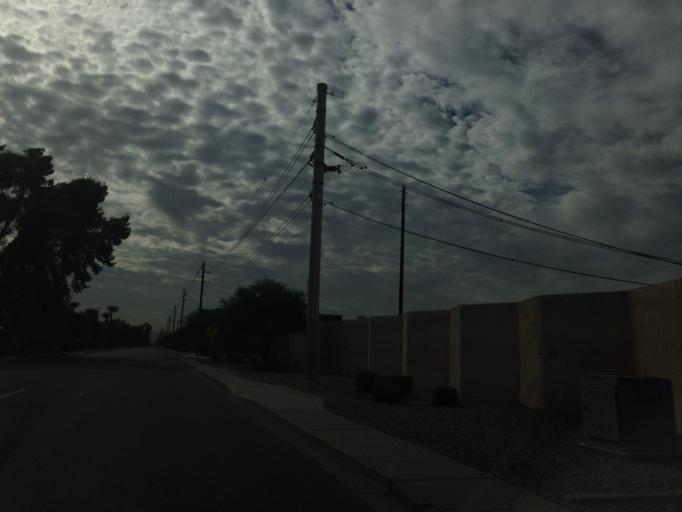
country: US
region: Arizona
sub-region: Maricopa County
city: Phoenix
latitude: 33.5068
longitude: -112.0216
